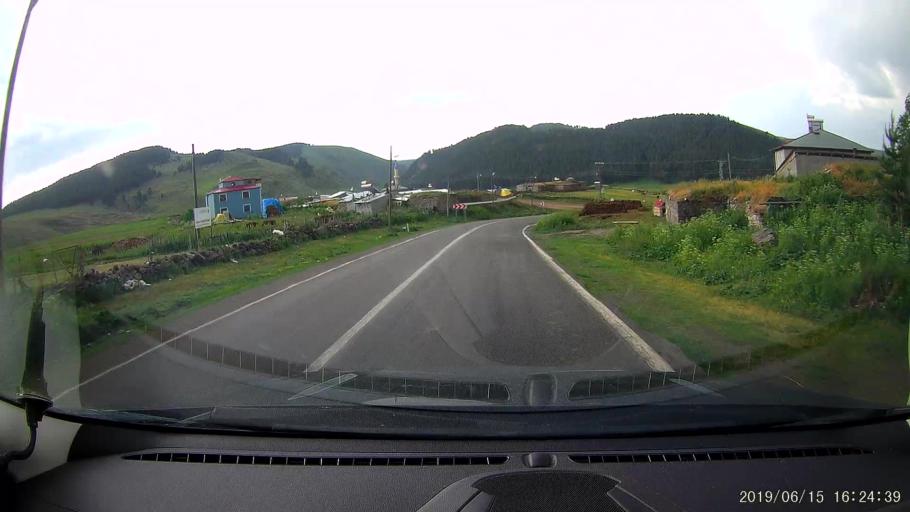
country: TR
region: Ardahan
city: Hanak
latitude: 41.1627
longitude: 42.8718
